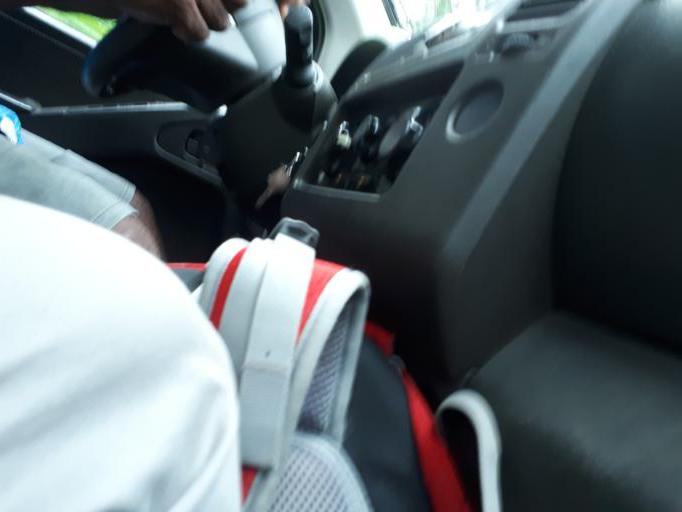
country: VU
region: Sanma
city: Luganville
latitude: -15.5726
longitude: 166.9404
